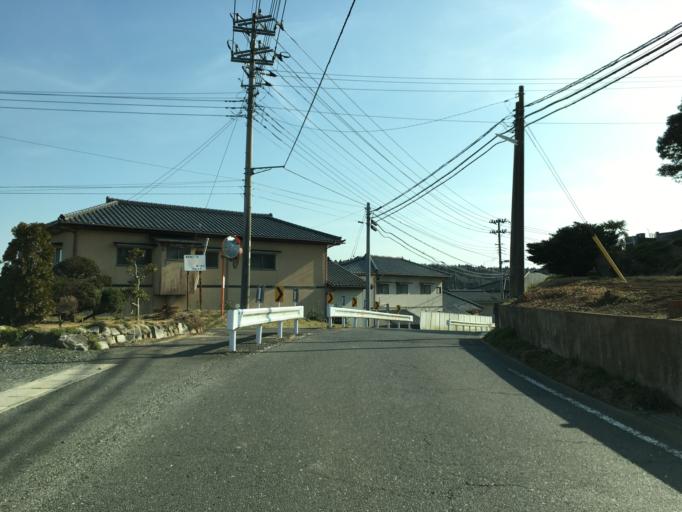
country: JP
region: Ibaraki
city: Kitaibaraki
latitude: 36.7628
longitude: 140.7212
